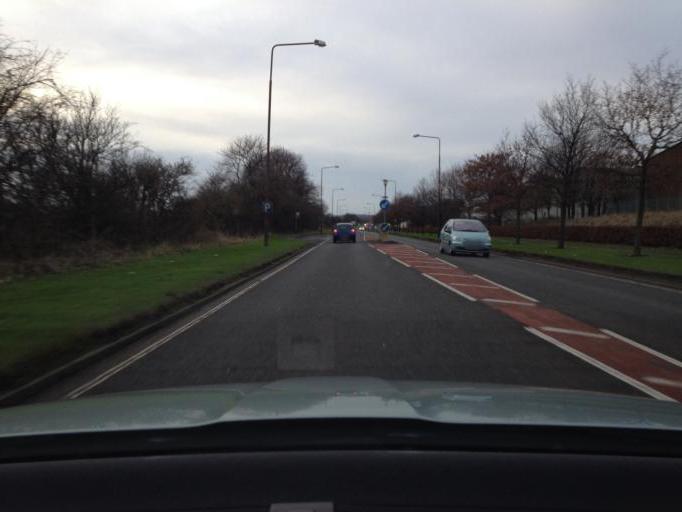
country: GB
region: Scotland
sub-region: West Lothian
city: Broxburn
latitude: 55.9360
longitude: -3.4408
